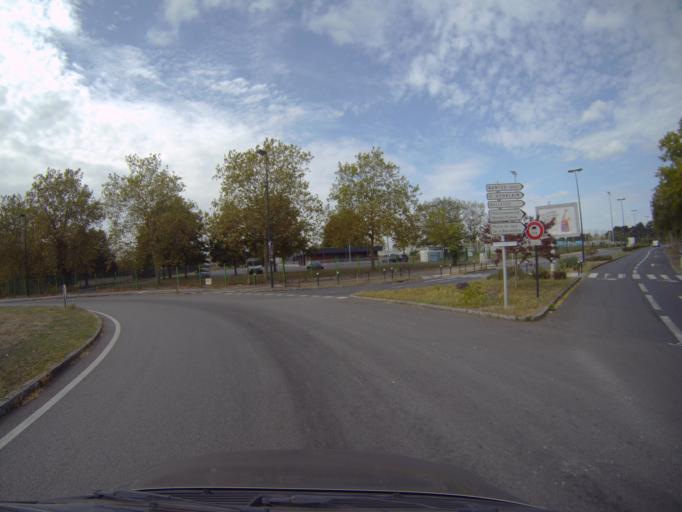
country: FR
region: Pays de la Loire
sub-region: Departement de la Loire-Atlantique
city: Bouguenais
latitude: 47.2008
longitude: -1.6137
